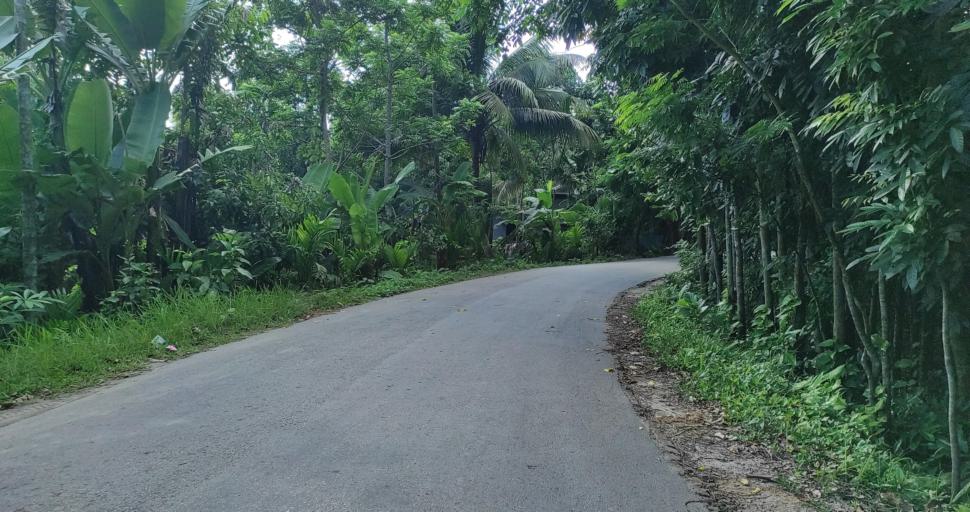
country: BD
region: Barisal
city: Gaurnadi
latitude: 22.8932
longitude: 90.1881
